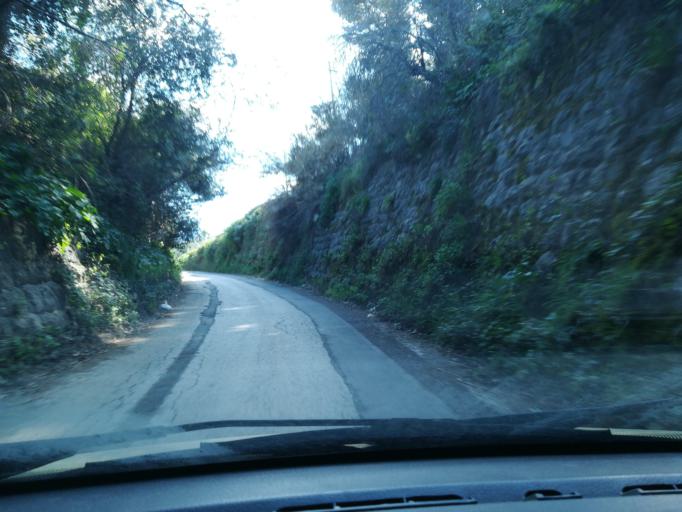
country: IT
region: Sicily
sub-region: Palermo
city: Cannizzaro-Favara
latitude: 38.0446
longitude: 13.2715
